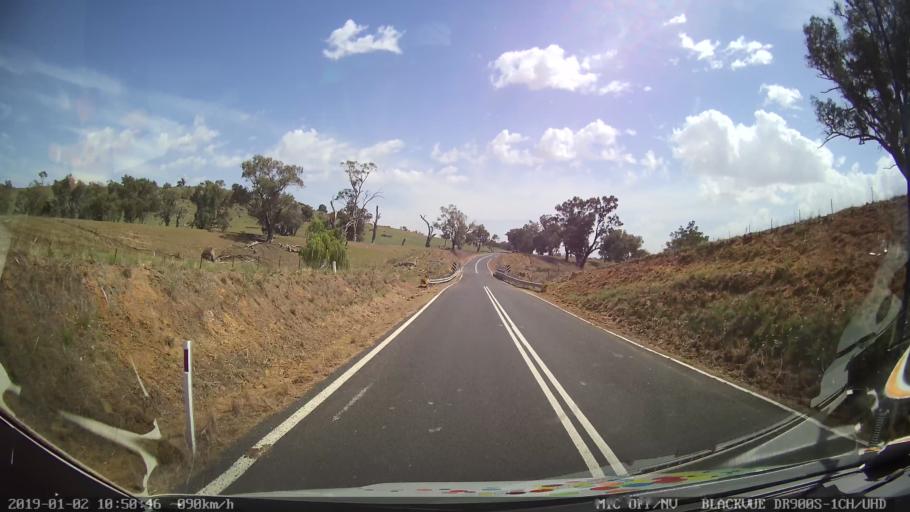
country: AU
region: New South Wales
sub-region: Cootamundra
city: Cootamundra
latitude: -34.7097
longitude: 148.2756
